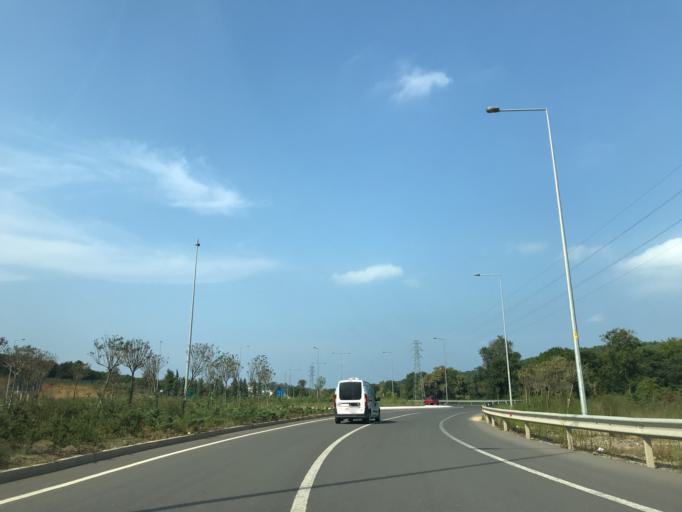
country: TR
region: Istanbul
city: Arikoey
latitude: 41.2357
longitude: 29.0414
